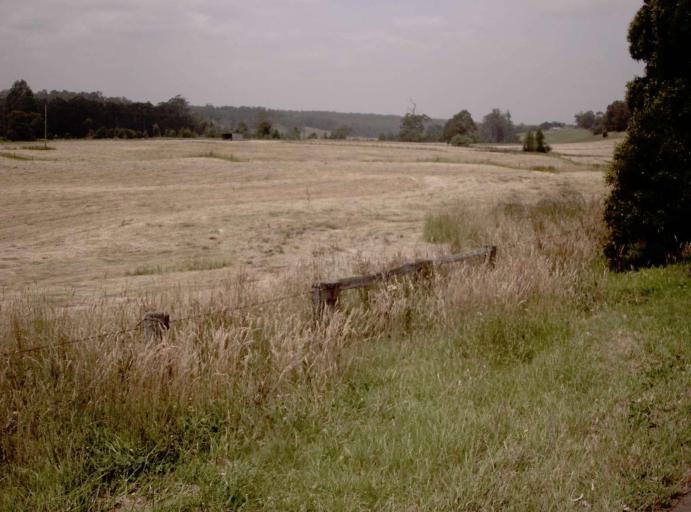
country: AU
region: Victoria
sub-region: Latrobe
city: Traralgon
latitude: -38.4379
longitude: 146.7322
